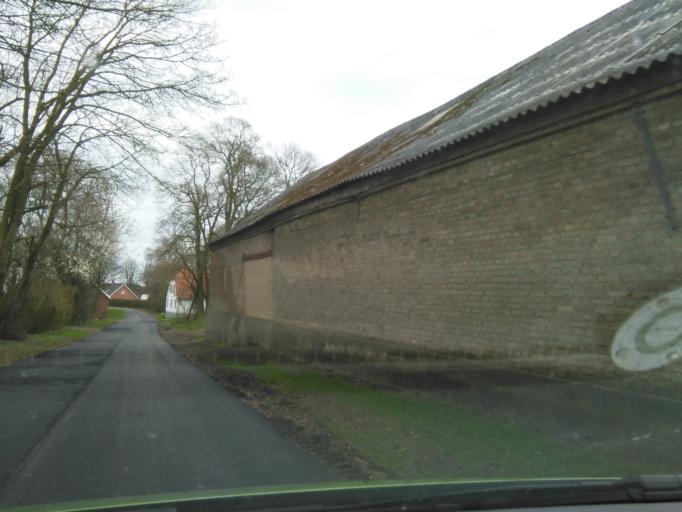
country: DK
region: Central Jutland
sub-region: Skanderborg Kommune
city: Stilling
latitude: 56.0817
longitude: 10.0003
